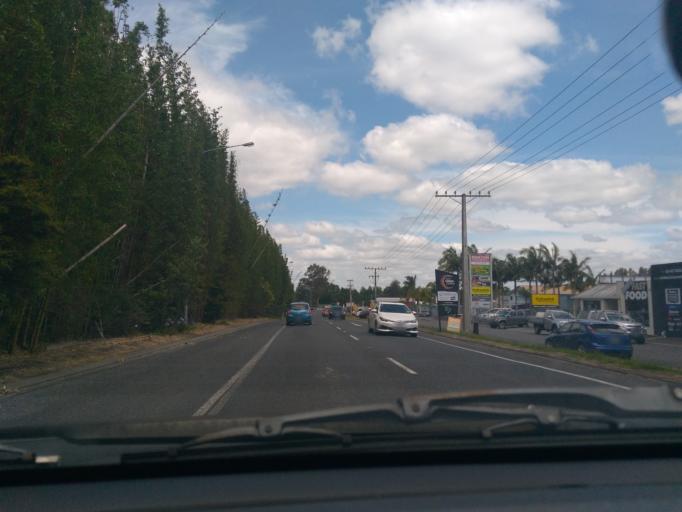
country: NZ
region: Northland
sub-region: Far North District
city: Kerikeri
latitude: -35.2069
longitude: 173.9181
